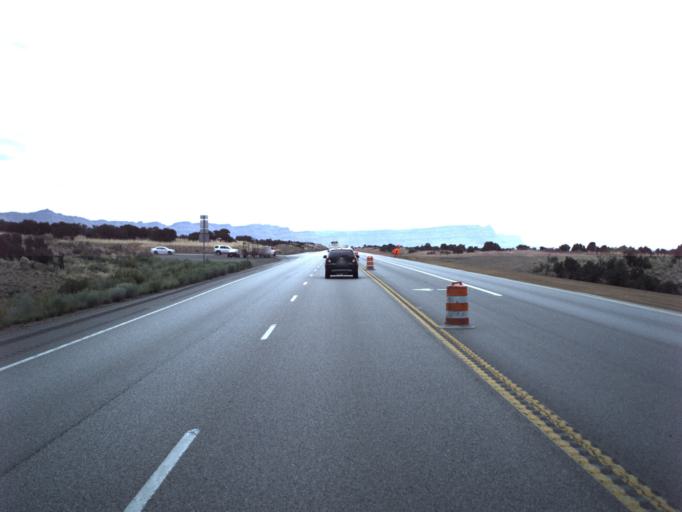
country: US
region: Utah
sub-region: Carbon County
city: East Carbon City
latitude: 39.4122
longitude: -110.4333
